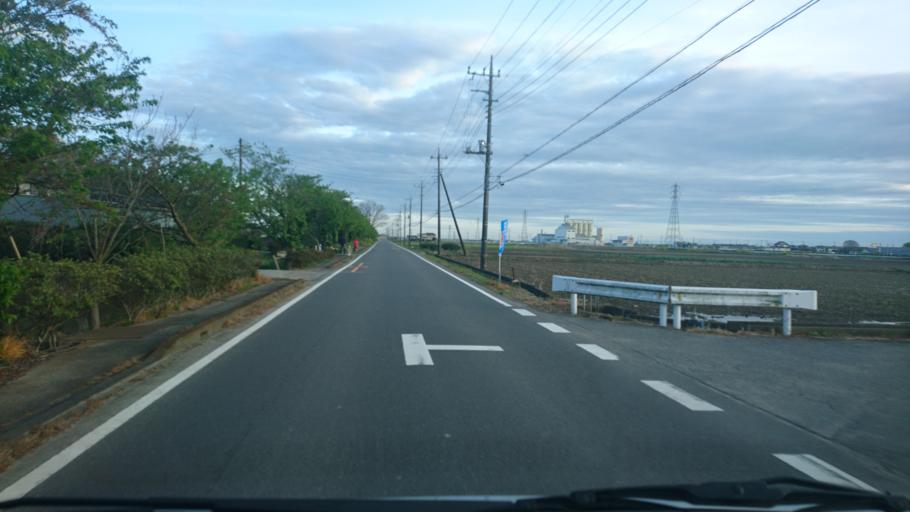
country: JP
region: Ibaraki
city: Mitsukaido
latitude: 36.0686
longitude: 139.9929
